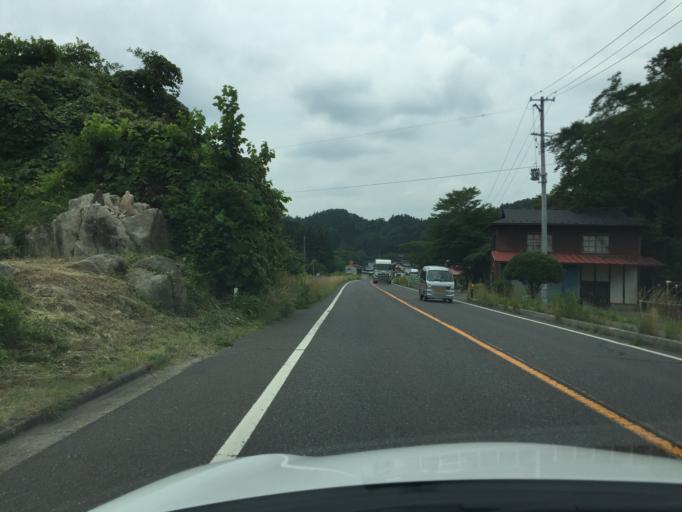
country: JP
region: Fukushima
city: Sukagawa
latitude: 37.3005
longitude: 140.5116
